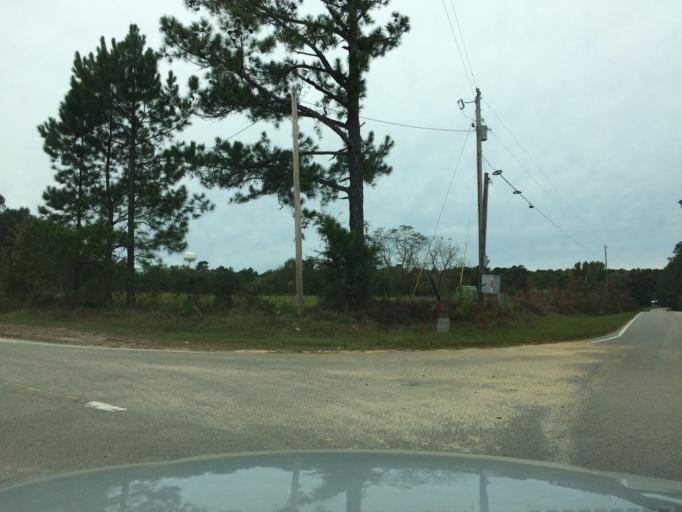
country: US
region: South Carolina
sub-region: Aiken County
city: New Ellenton
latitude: 33.4641
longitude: -81.6779
